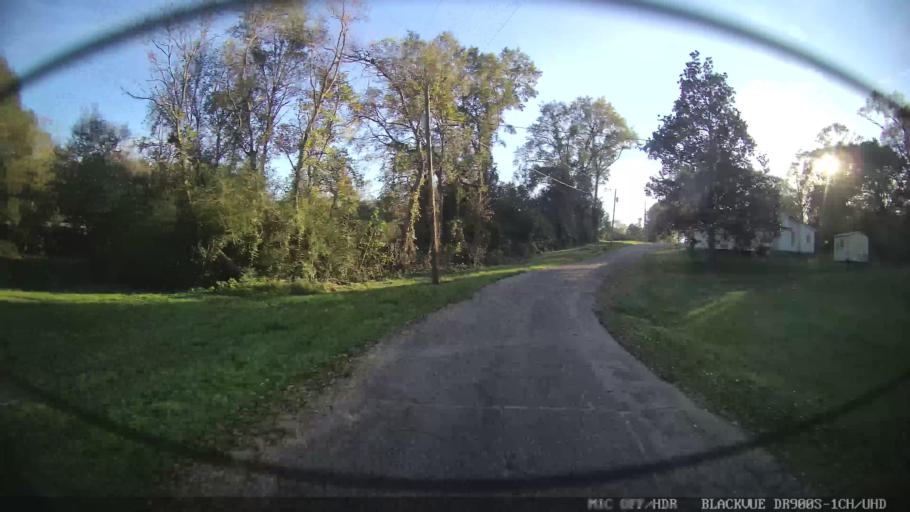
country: US
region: Mississippi
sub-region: Lamar County
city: Purvis
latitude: 31.1474
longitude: -89.4101
